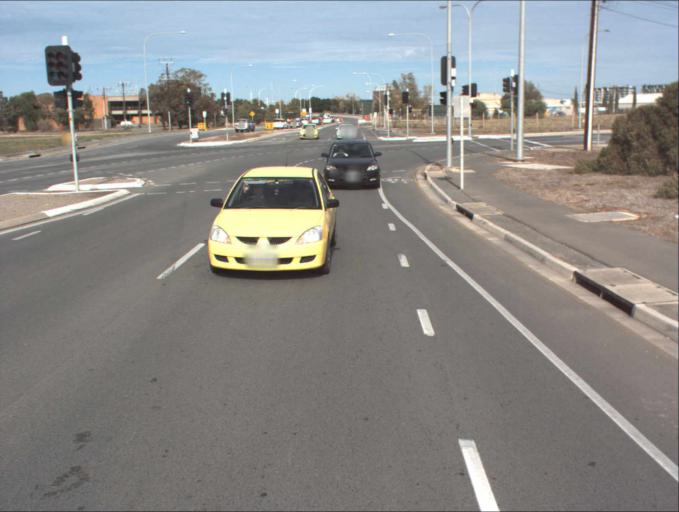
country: AU
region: South Australia
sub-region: Port Adelaide Enfield
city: Birkenhead
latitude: -34.8387
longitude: 138.5023
